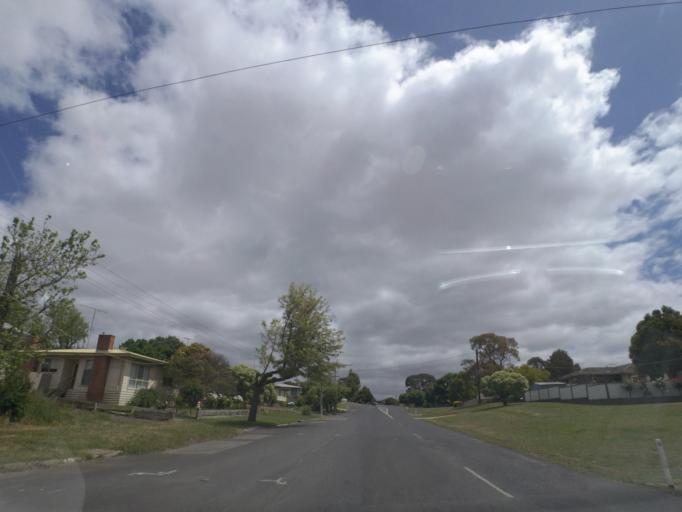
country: AU
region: Victoria
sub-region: Whittlesea
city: Whittlesea
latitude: -37.2106
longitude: 145.0466
